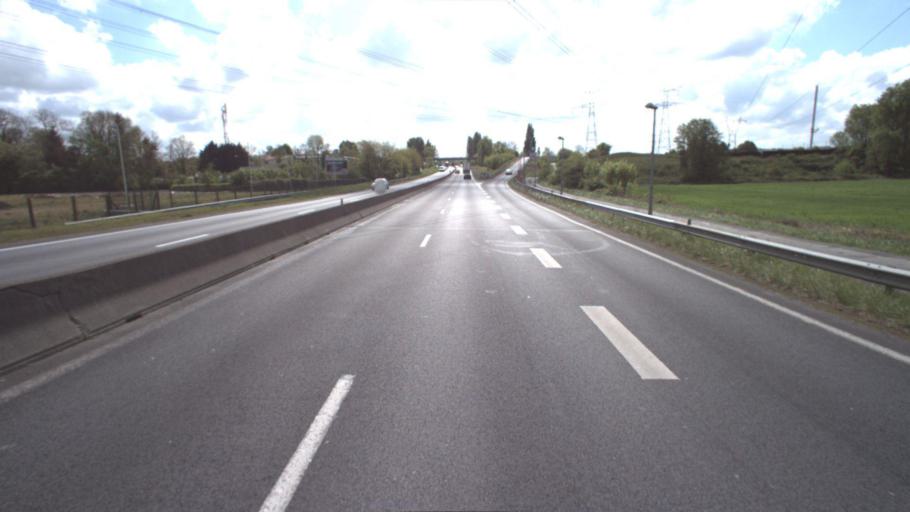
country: FR
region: Ile-de-France
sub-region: Departement de Seine-et-Marne
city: Ozoir-la-Ferriere
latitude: 48.7637
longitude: 2.6593
